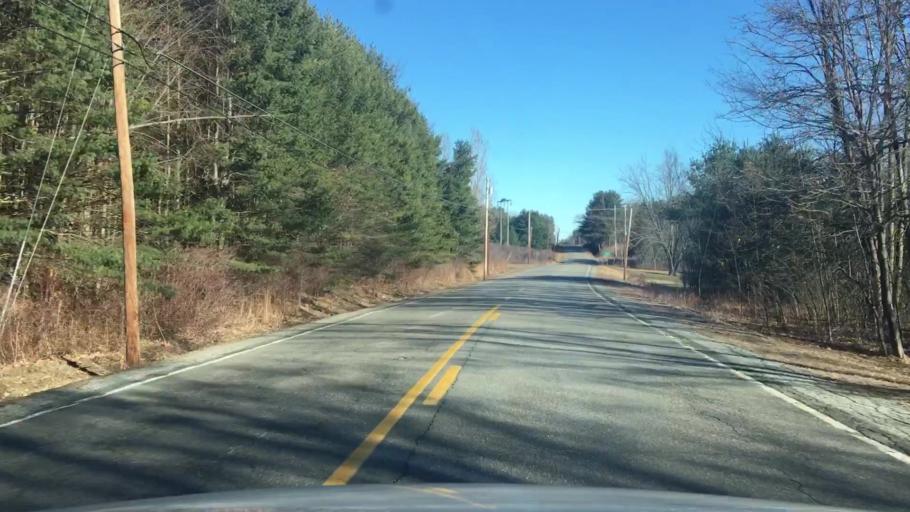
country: US
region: Maine
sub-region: Kennebec County
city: Benton
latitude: 44.5709
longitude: -69.5695
